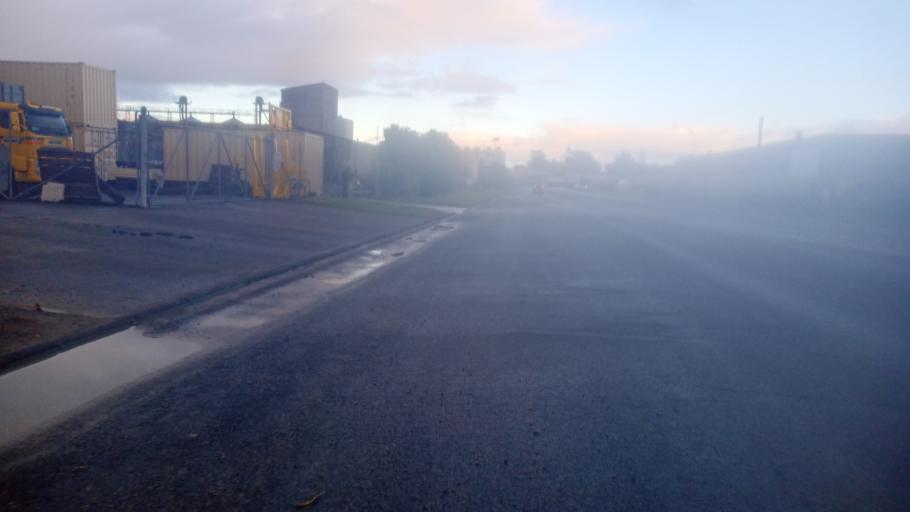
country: NZ
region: Gisborne
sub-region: Gisborne District
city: Gisborne
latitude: -38.6676
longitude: 178.0010
